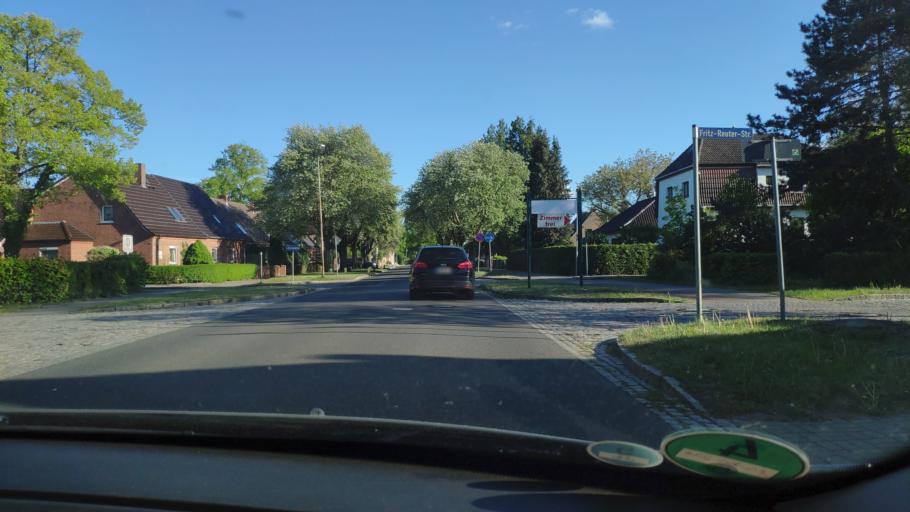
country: DE
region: Mecklenburg-Vorpommern
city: Rechlin
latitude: 53.2805
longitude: 12.8149
